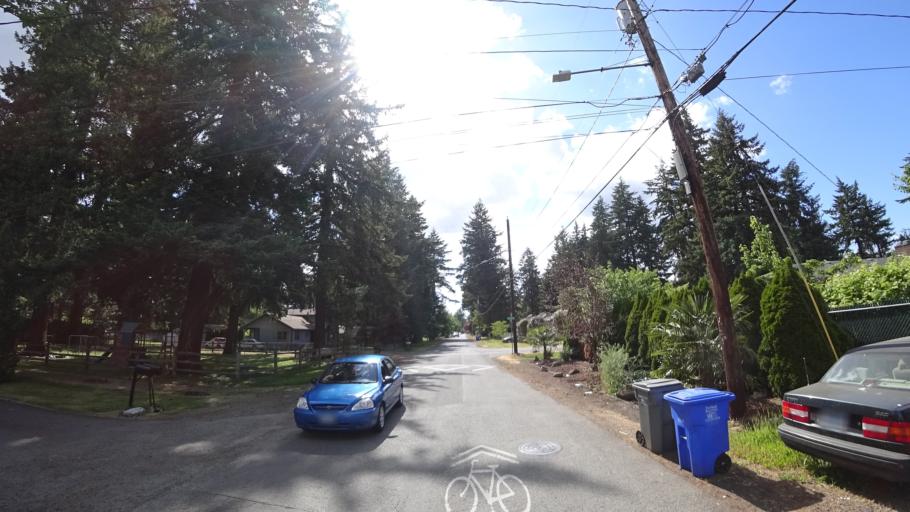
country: US
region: Oregon
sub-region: Multnomah County
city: Lents
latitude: 45.4945
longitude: -122.5401
